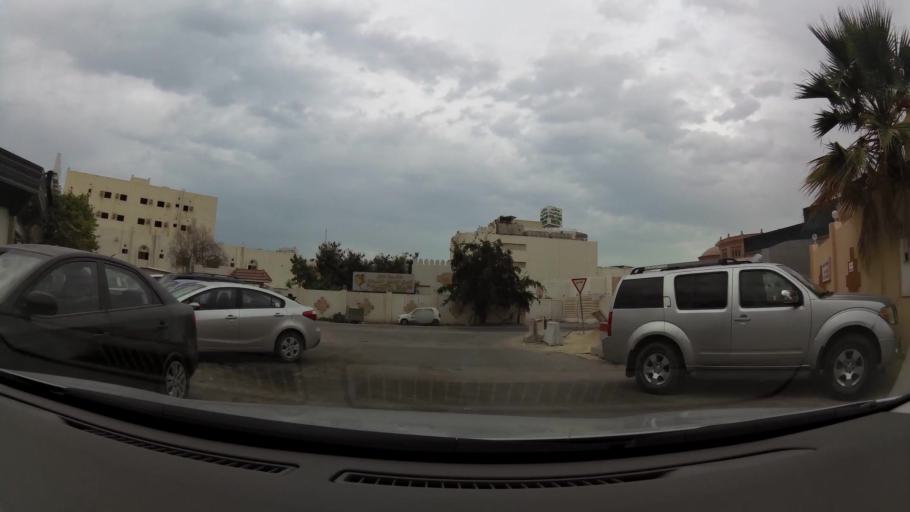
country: QA
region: Baladiyat ad Dawhah
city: Doha
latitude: 25.2744
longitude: 51.5019
